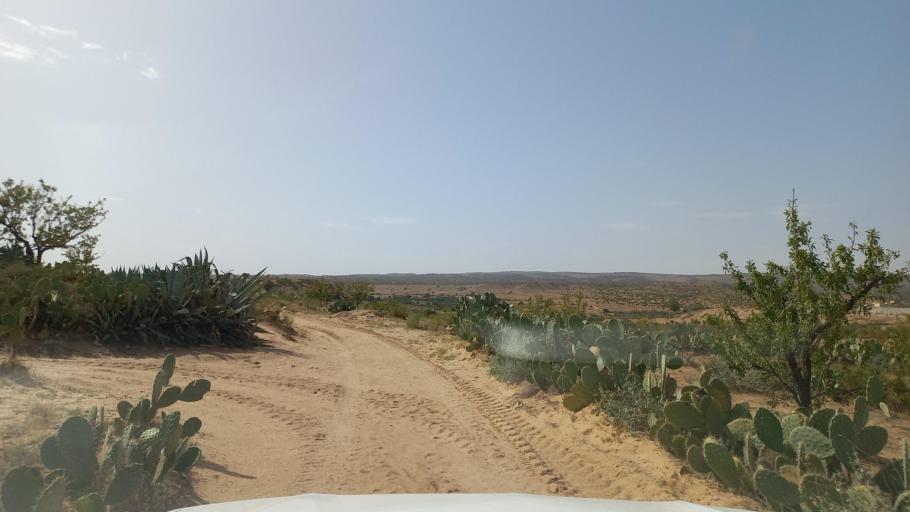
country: TN
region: Al Qasrayn
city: Kasserine
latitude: 35.2998
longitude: 8.9466
